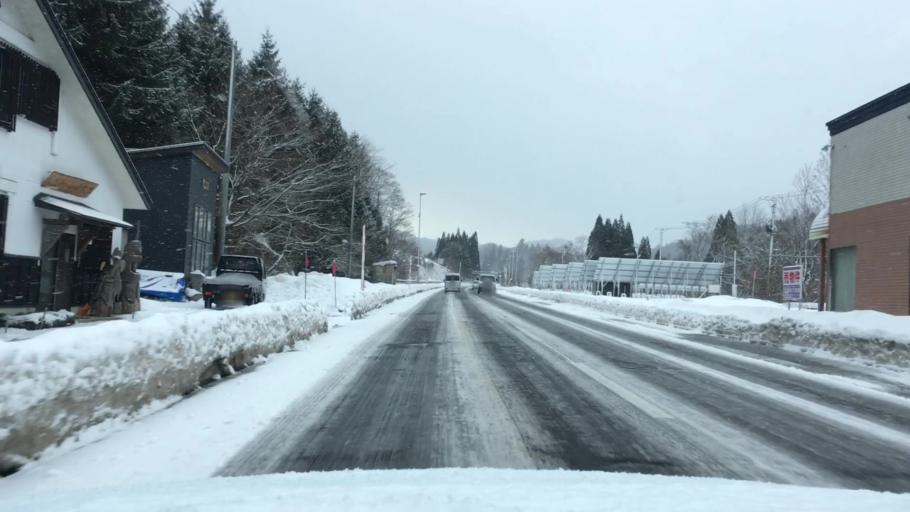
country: JP
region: Aomori
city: Kuroishi
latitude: 40.4578
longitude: 140.6359
